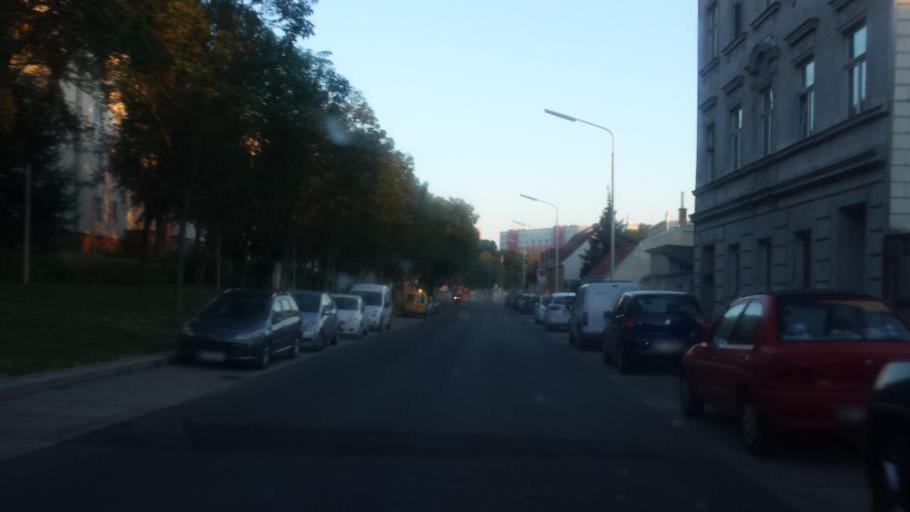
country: AT
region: Lower Austria
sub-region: Politischer Bezirk Wien-Umgebung
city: Schwechat
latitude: 48.1746
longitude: 16.4267
